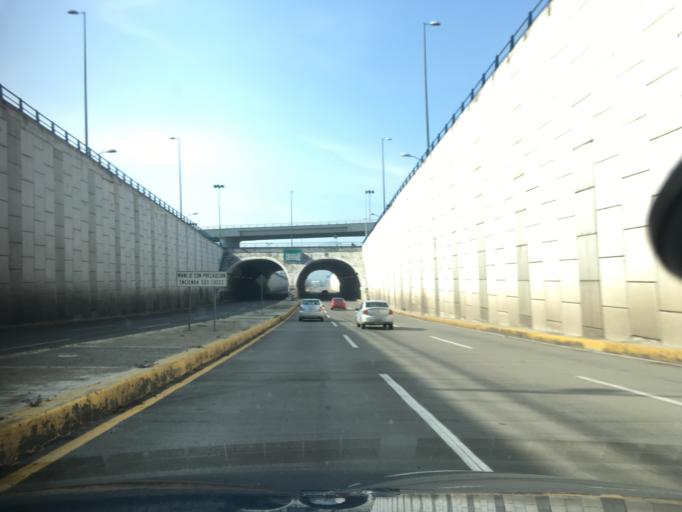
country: MX
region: Michoacan
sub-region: Morelia
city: San Antonio
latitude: 19.7017
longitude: -101.2442
